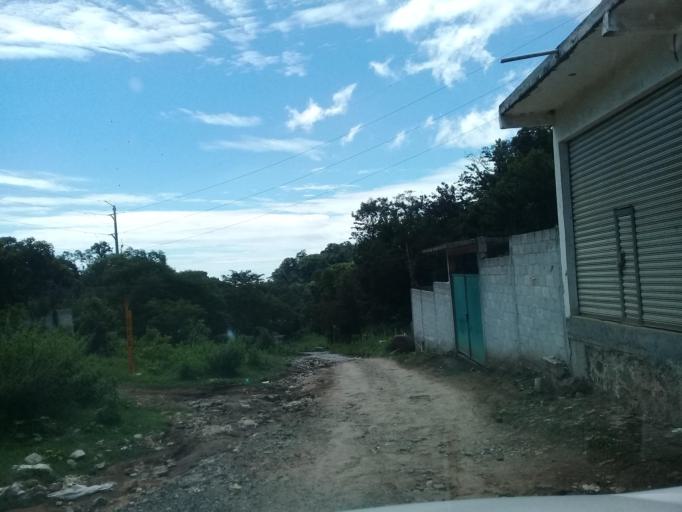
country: MX
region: Veracruz
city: El Castillo
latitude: 19.5707
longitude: -96.8875
